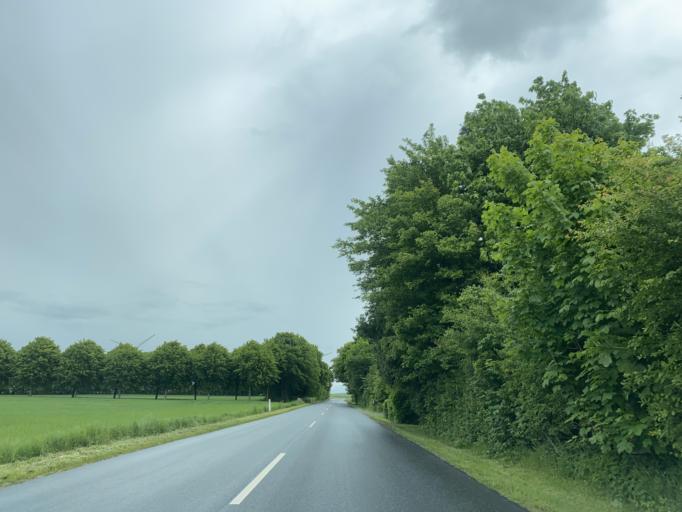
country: DK
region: Central Jutland
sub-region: Arhus Kommune
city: Sabro
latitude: 56.2540
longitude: 9.9732
